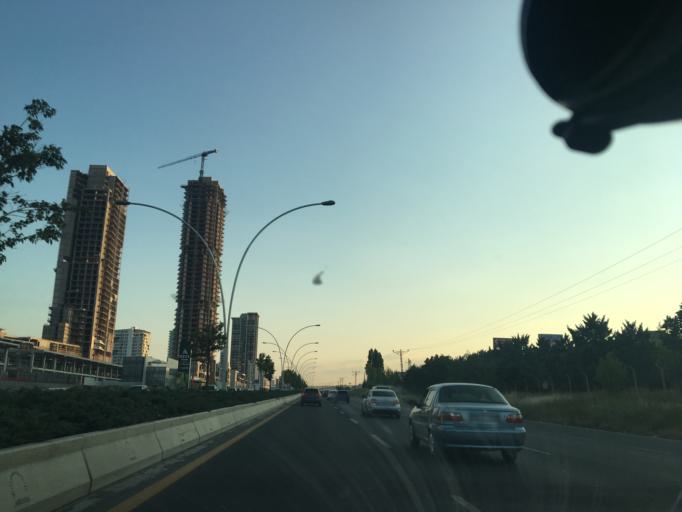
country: TR
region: Ankara
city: Etimesgut
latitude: 39.8791
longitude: 32.6553
